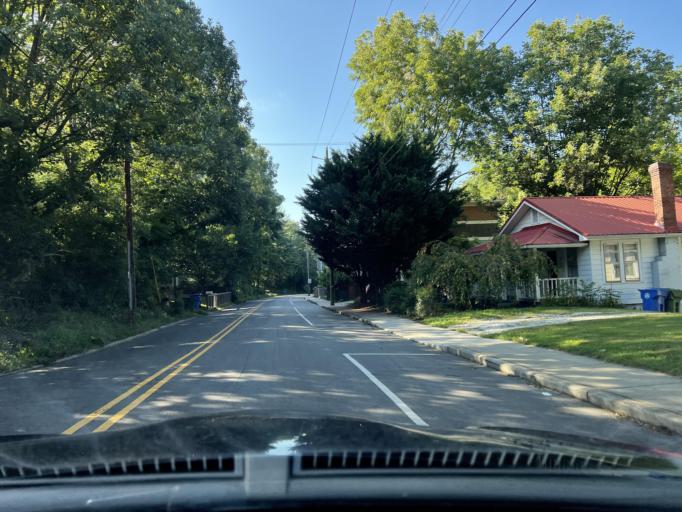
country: US
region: North Carolina
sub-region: Buncombe County
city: Asheville
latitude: 35.5754
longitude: -82.5850
